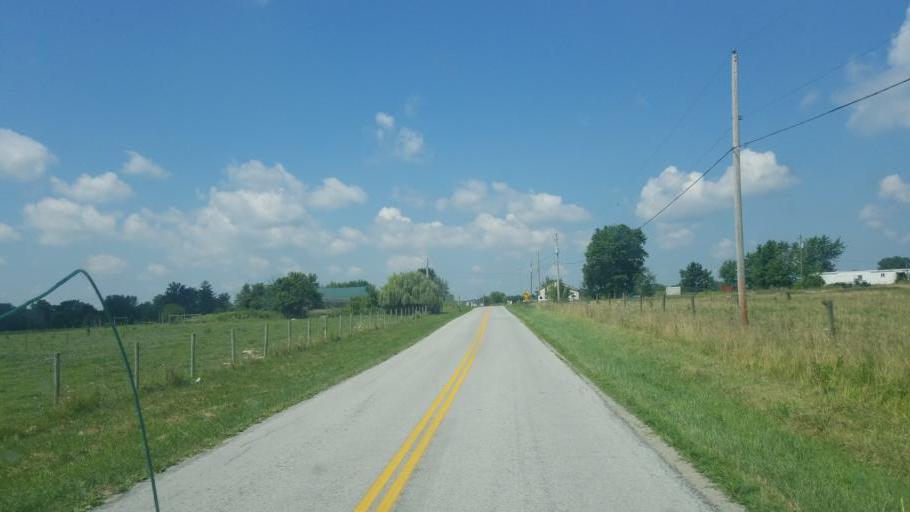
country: US
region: Ohio
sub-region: Allen County
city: Lima
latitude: 40.6987
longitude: -83.9623
